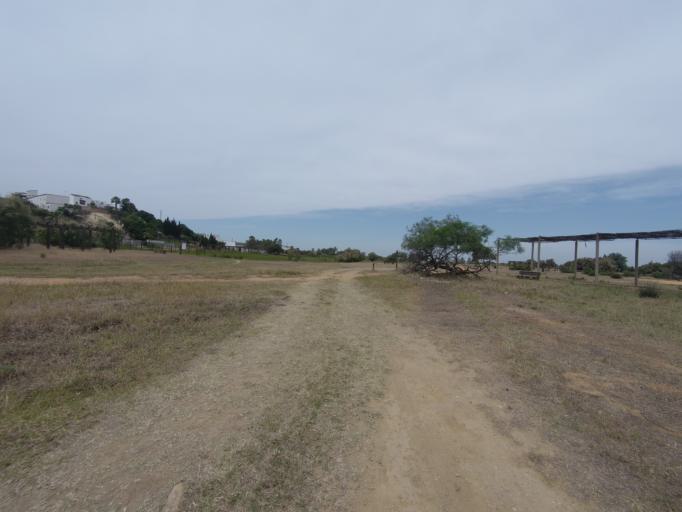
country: ES
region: Andalusia
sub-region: Provincia de Huelva
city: Palos de la Frontera
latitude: 37.2326
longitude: -6.8944
